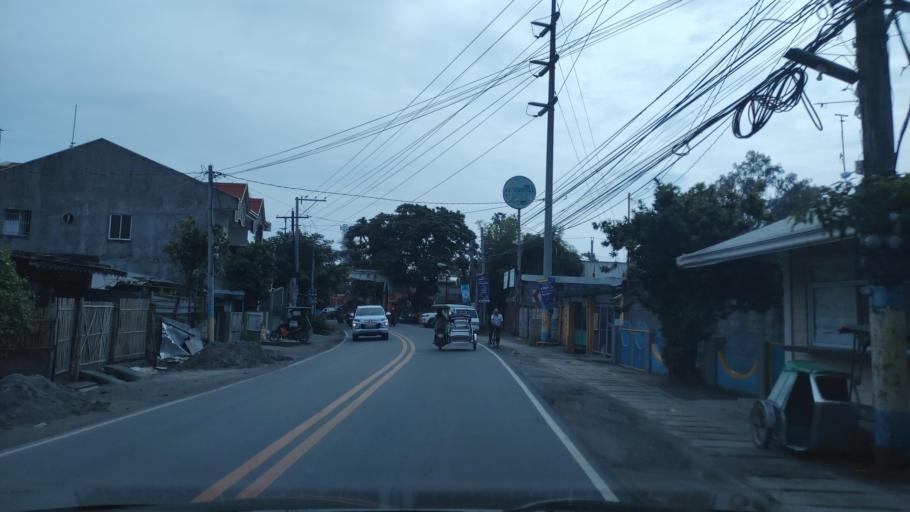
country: PH
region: Central Luzon
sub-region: Province of Pampanga
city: Santa Ana
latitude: 15.1182
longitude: 120.7755
